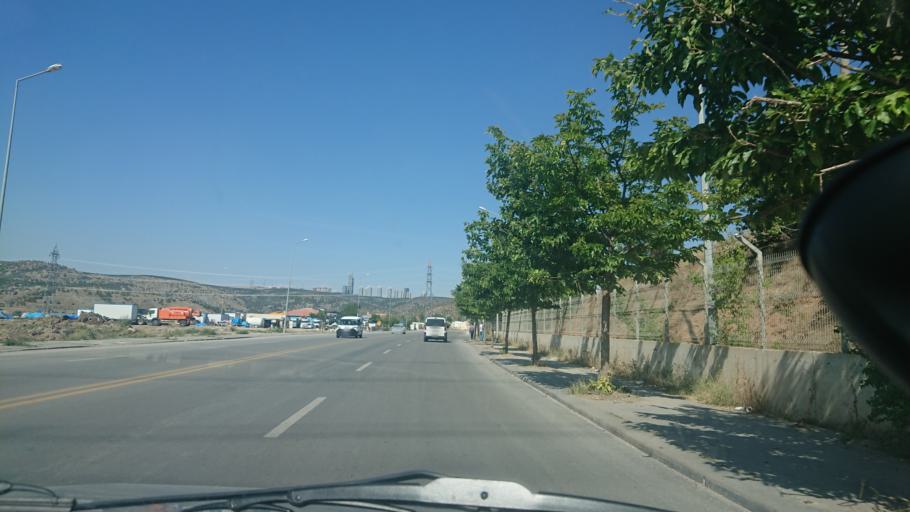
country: TR
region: Ankara
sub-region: Goelbasi
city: Golbasi
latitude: 39.8049
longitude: 32.8145
